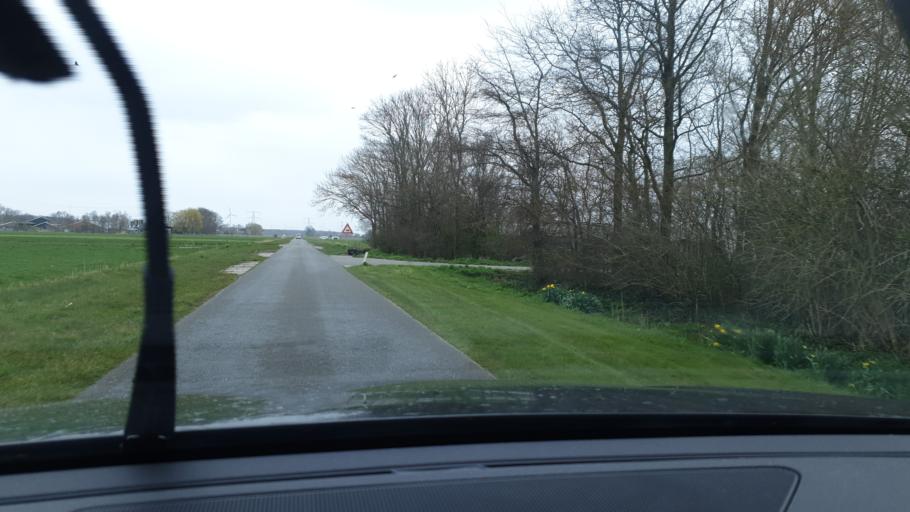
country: NL
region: Flevoland
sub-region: Gemeente Lelystad
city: Lelystad
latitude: 52.5694
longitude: 5.5459
